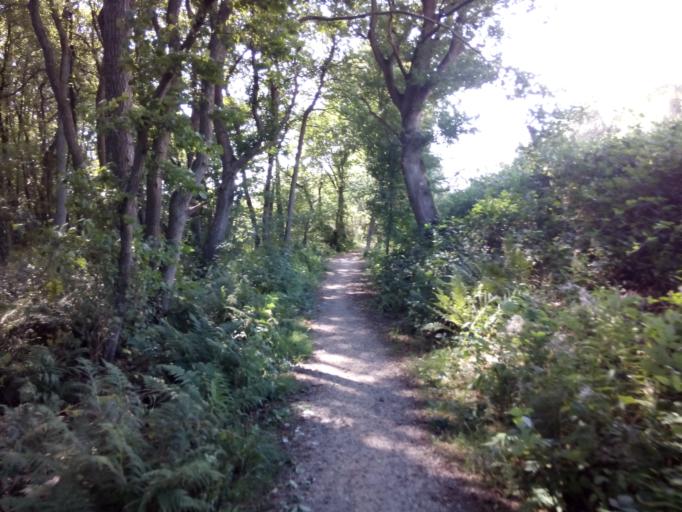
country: DK
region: Central Jutland
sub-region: Skanderborg Kommune
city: Ry
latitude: 56.0956
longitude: 9.7449
